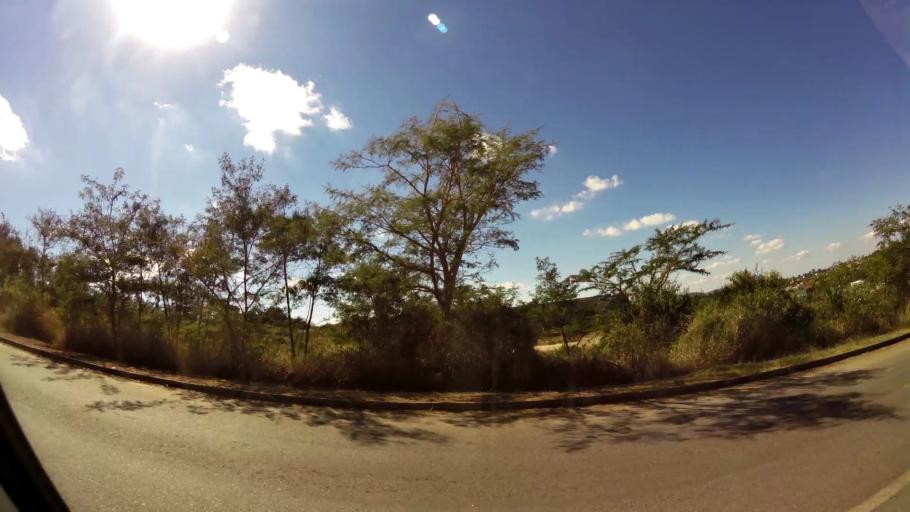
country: ZA
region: Limpopo
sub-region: Mopani District Municipality
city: Tzaneen
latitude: -23.8237
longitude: 30.1539
